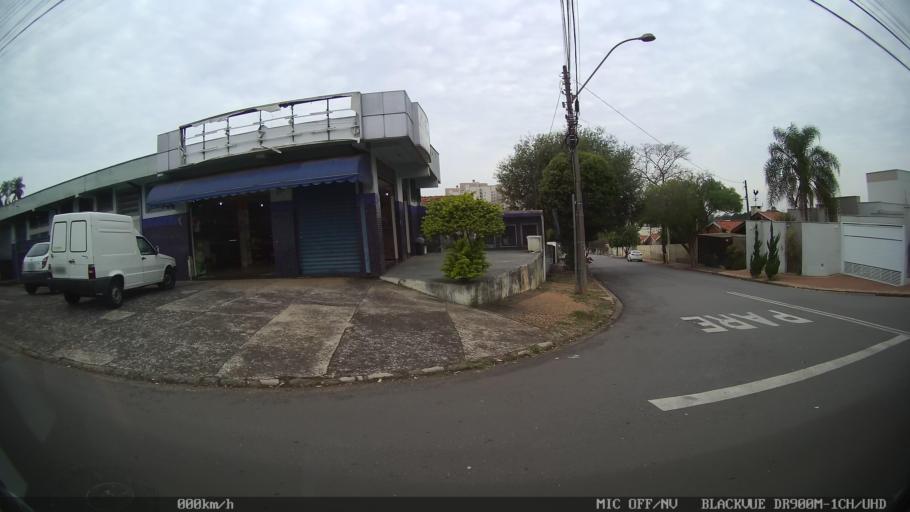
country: BR
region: Sao Paulo
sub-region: Americana
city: Americana
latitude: -22.7559
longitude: -47.3316
